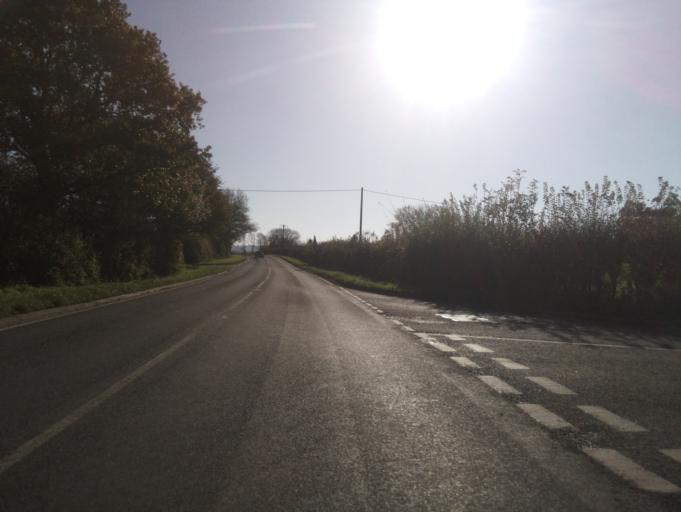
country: GB
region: England
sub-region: Dorset
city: Sherborne
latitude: 50.8910
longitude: -2.4918
